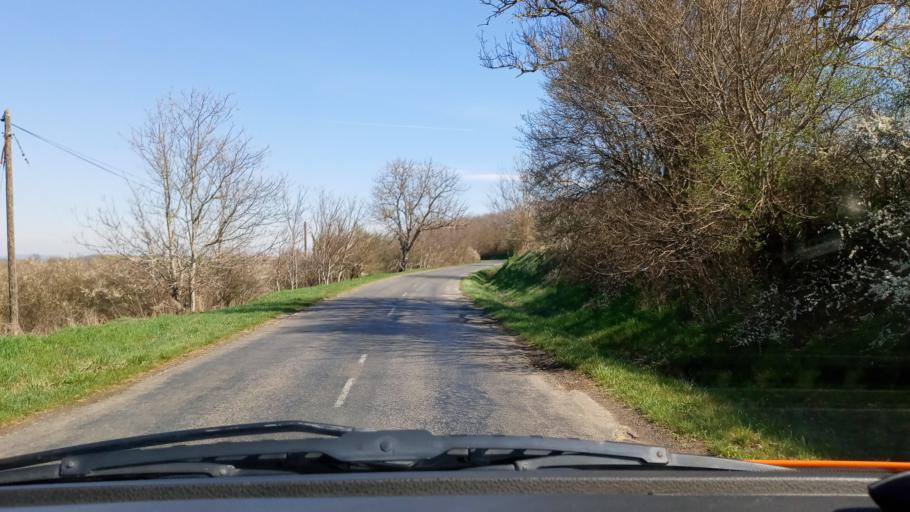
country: HU
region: Baranya
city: Boly
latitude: 46.0156
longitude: 18.4544
